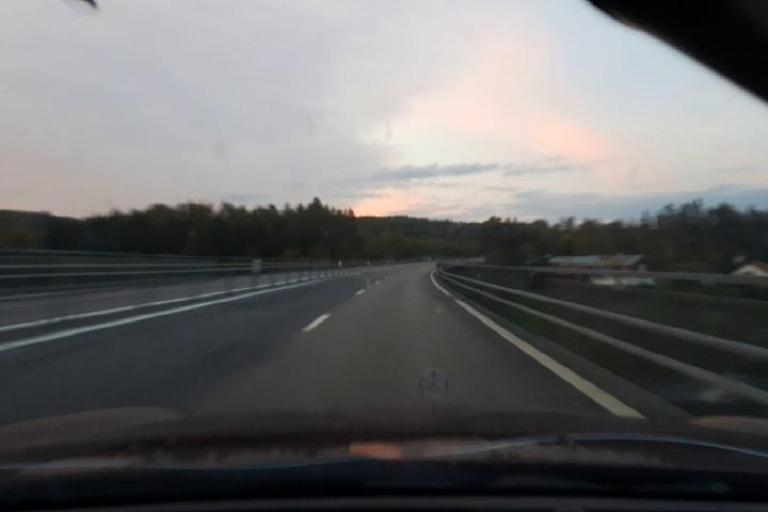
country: SE
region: Vaesternorrland
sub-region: Haernoesands Kommun
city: Haernoesand
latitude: 62.8379
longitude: 17.9705
